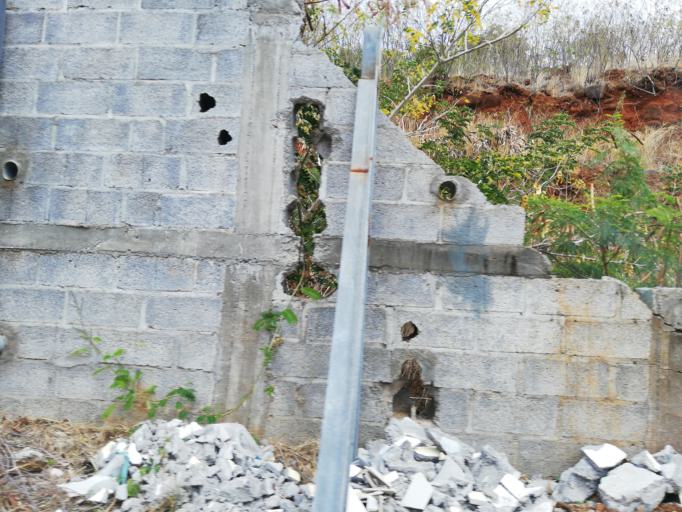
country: MU
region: Moka
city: Pailles
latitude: -20.1944
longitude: 57.4719
